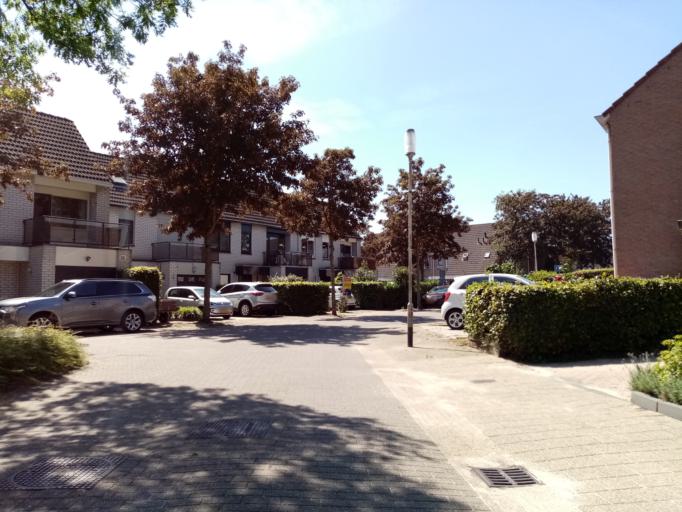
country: NL
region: North Brabant
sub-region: Gemeente Breda
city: Breda
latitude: 51.6125
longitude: 4.7284
